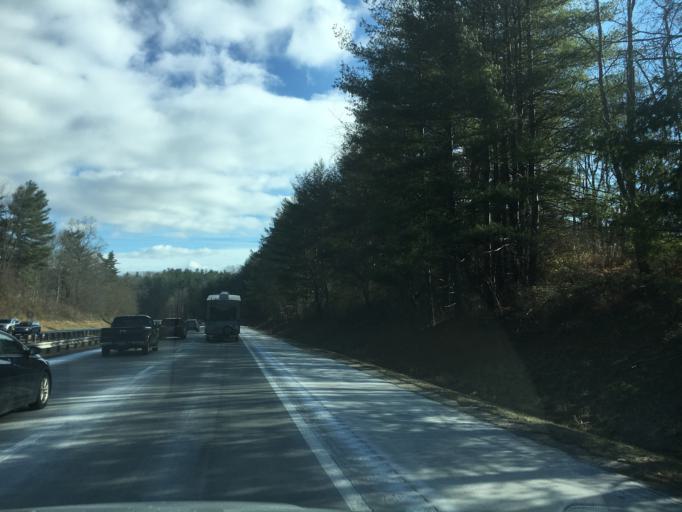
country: US
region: North Carolina
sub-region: Buncombe County
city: Asheville
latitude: 35.5608
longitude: -82.5710
